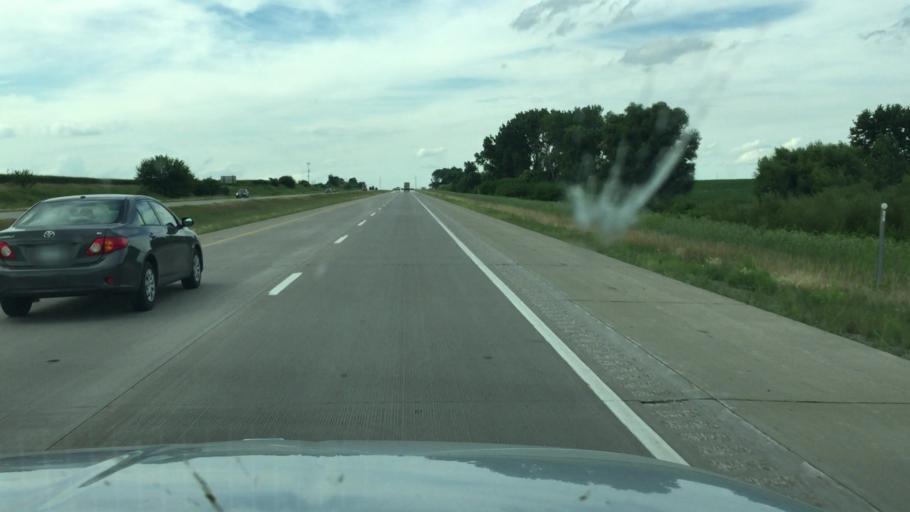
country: US
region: Iowa
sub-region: Scott County
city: Walcott
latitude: 41.5589
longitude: -90.6783
